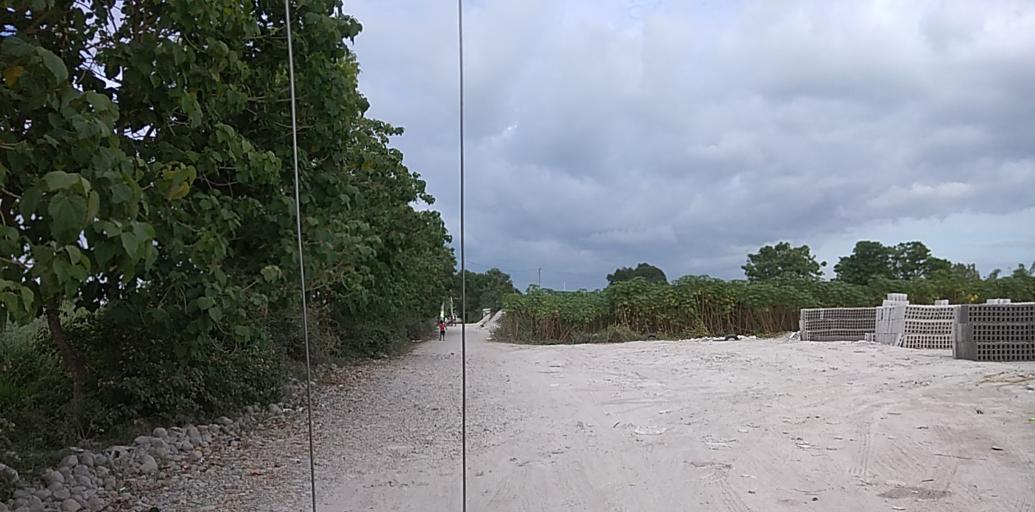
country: PH
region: Central Luzon
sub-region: Province of Pampanga
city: Pulung Santol
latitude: 15.0574
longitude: 120.5650
